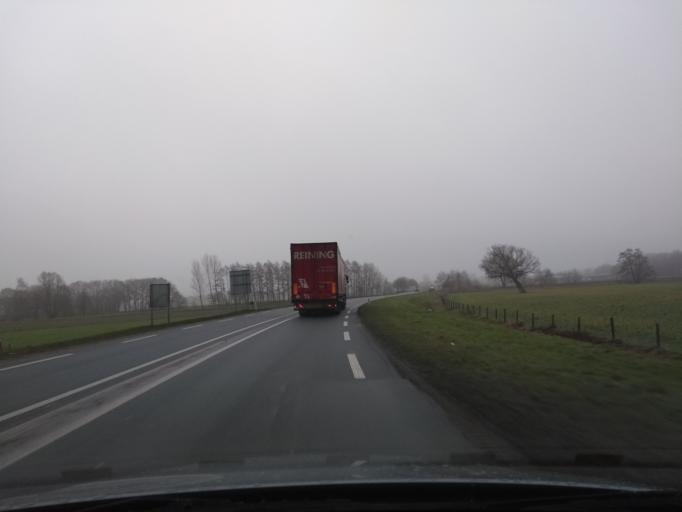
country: NL
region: Overijssel
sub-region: Gemeente Wierden
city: Wierden
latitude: 52.3206
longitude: 6.5436
